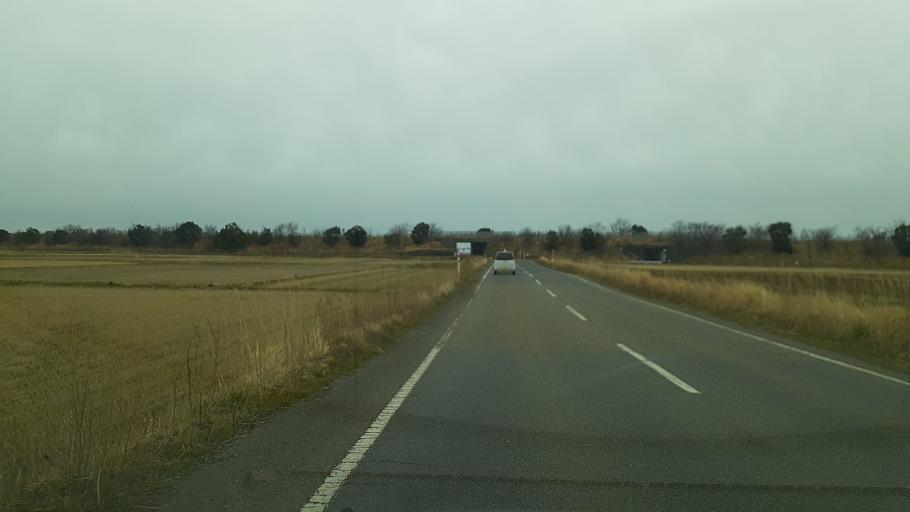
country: JP
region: Niigata
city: Niitsu-honcho
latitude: 37.8206
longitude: 139.0845
